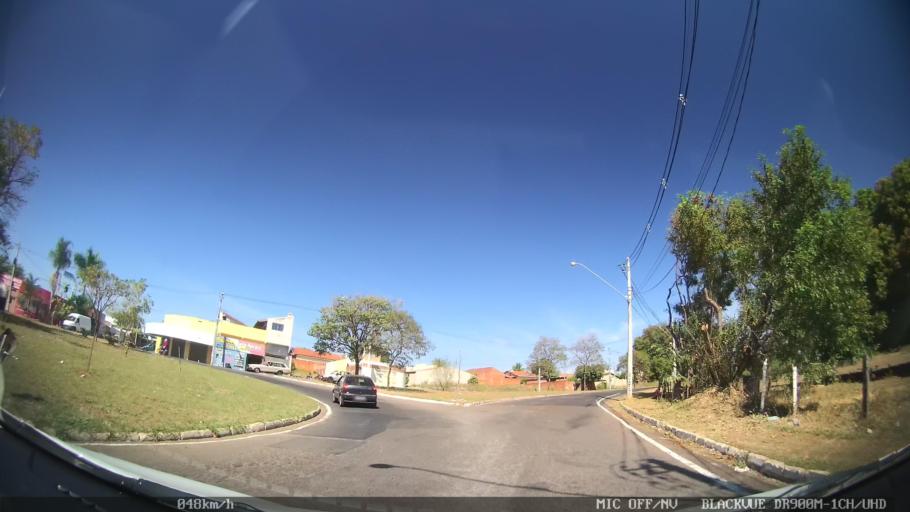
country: BR
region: Sao Paulo
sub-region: Sao Jose Do Rio Preto
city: Sao Jose do Rio Preto
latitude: -20.7590
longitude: -49.4034
